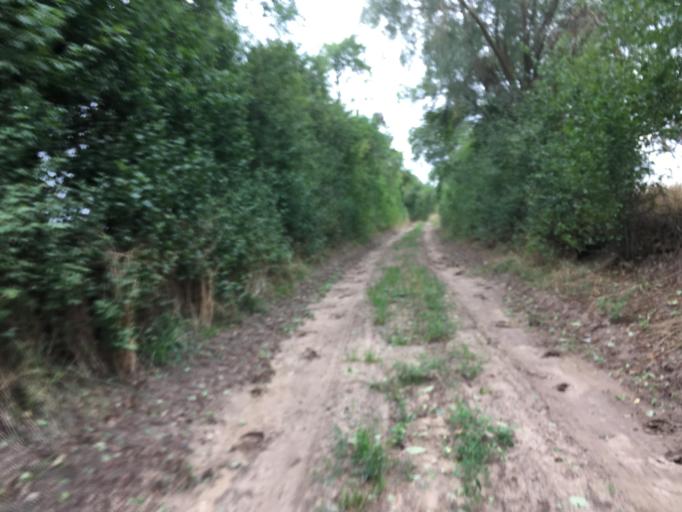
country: DE
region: Brandenburg
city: Passow
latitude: 53.1326
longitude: 14.1104
